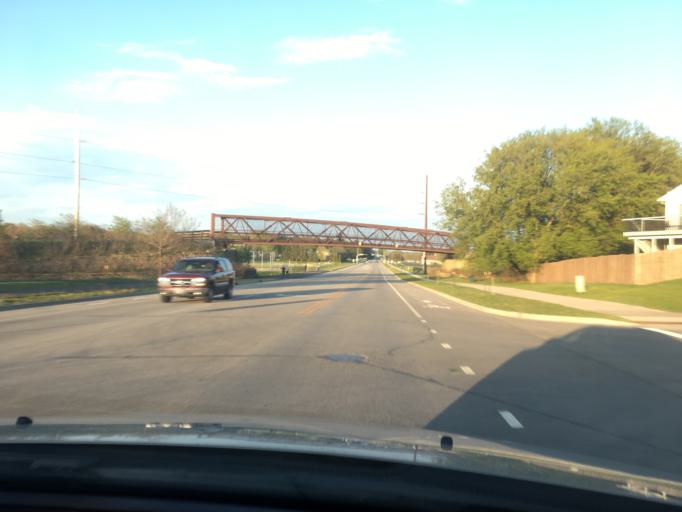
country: US
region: Minnesota
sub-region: Olmsted County
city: Oronoco
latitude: 44.0794
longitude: -92.5347
